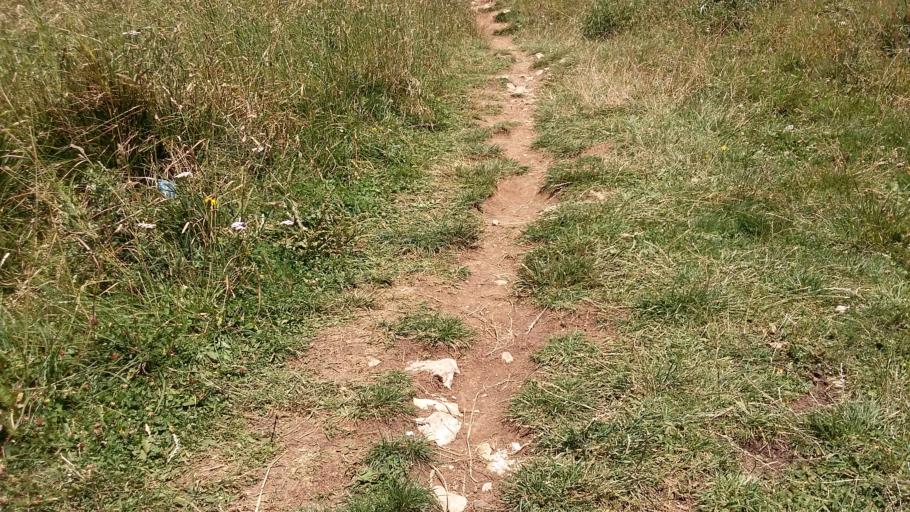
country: IT
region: Trentino-Alto Adige
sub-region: Provincia di Trento
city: Brentonico
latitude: 45.7993
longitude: 10.8936
